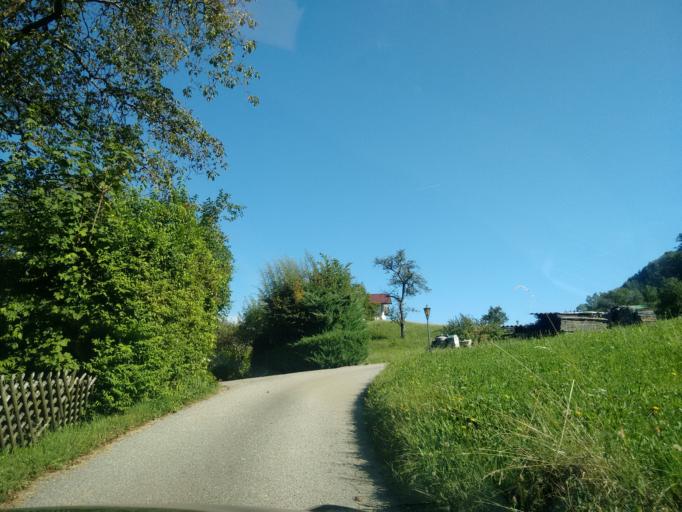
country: AT
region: Upper Austria
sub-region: Politischer Bezirk Vocklabruck
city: Steinbach am Attersee
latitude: 47.8416
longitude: 13.5481
